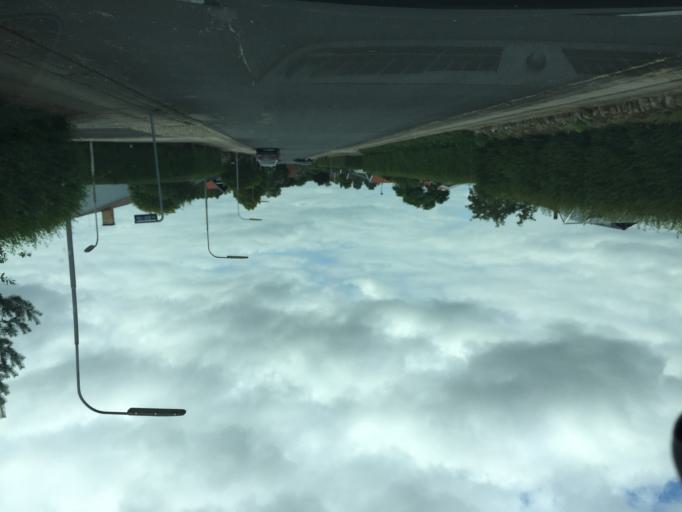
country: DK
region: South Denmark
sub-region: Odense Kommune
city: Hojby
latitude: 55.3400
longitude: 10.4273
